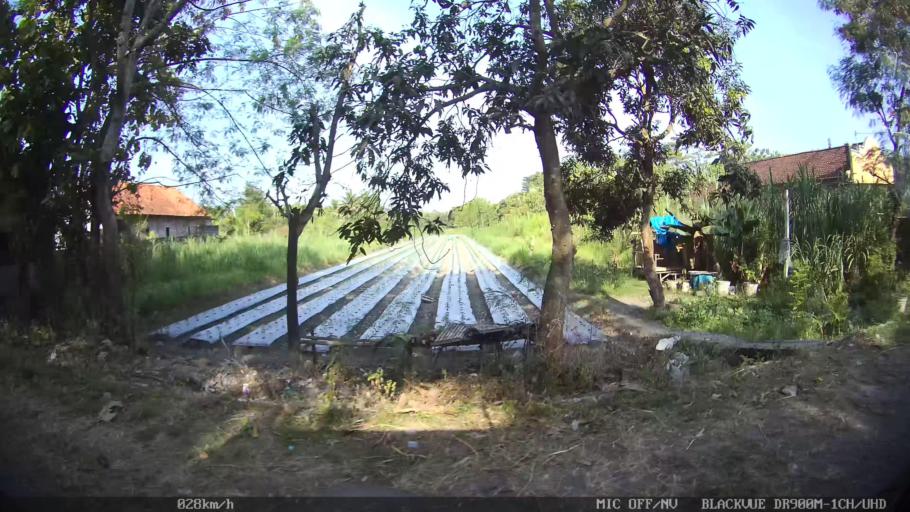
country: ID
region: Daerah Istimewa Yogyakarta
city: Bantul
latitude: -7.8851
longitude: 110.3048
